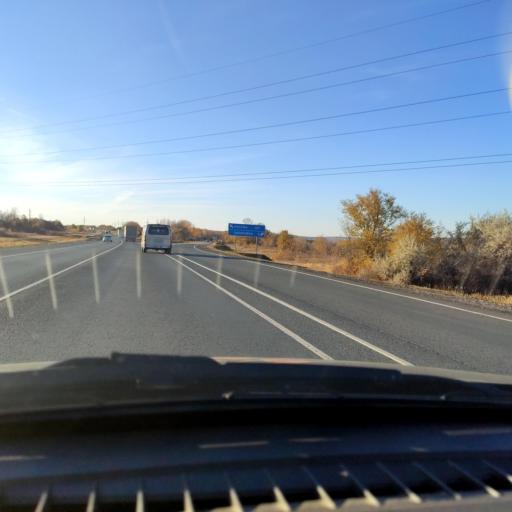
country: RU
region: Samara
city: Varlamovo
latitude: 53.1941
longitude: 48.3293
